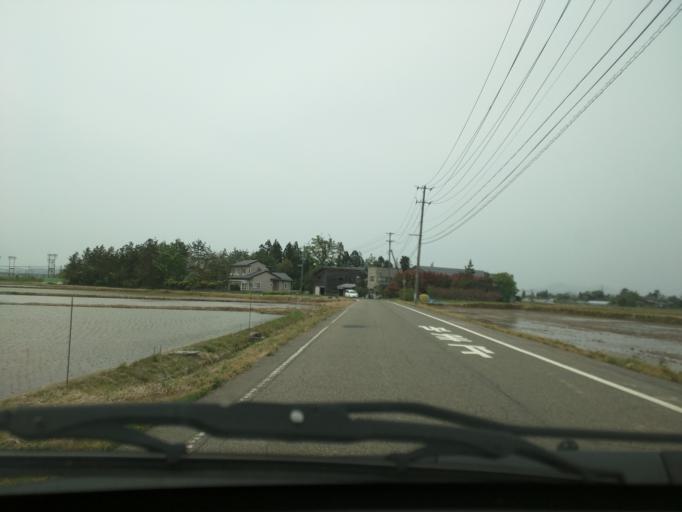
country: JP
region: Niigata
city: Mitsuke
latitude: 37.5495
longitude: 138.9154
